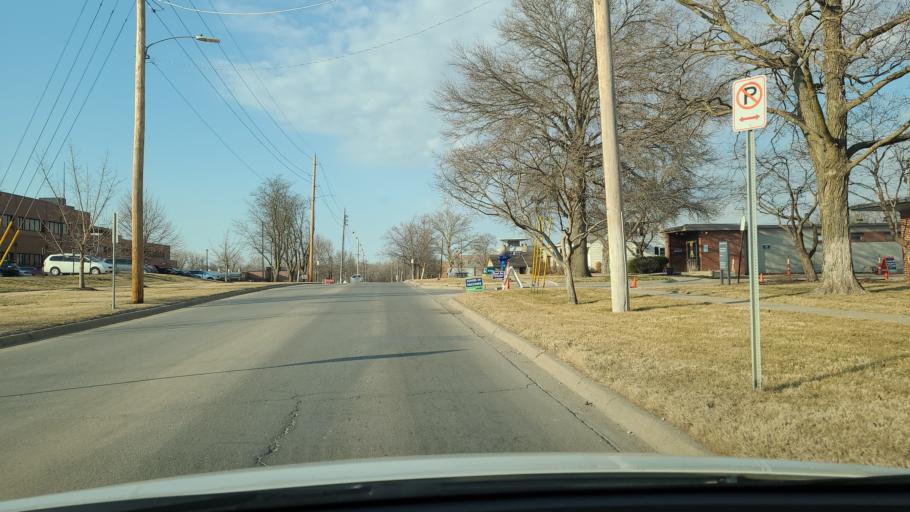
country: US
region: Kansas
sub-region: Douglas County
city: Lawrence
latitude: 38.9773
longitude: -95.2476
